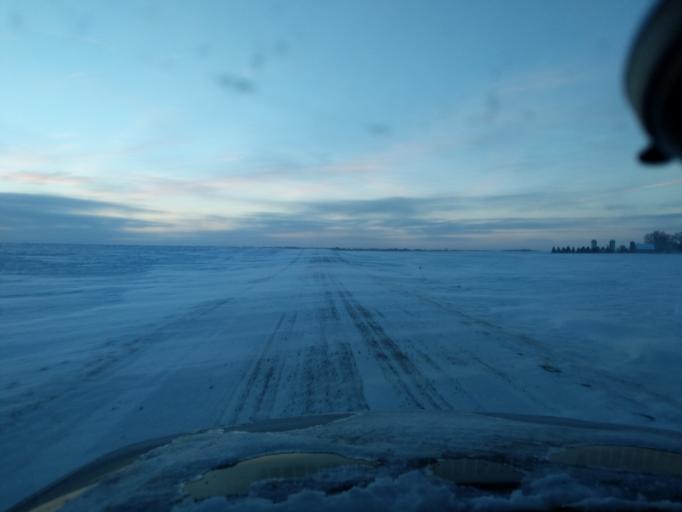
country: US
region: Minnesota
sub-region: Renville County
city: Renville
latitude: 44.7271
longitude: -95.3509
